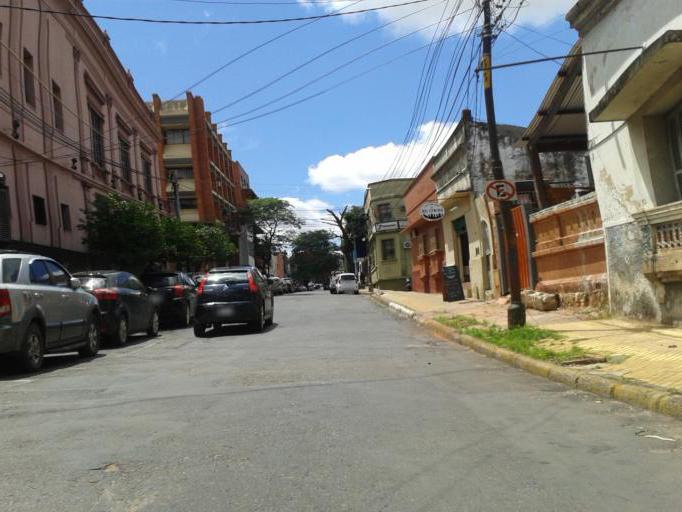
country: PY
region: Asuncion
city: Asuncion
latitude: -25.2881
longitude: -57.6359
